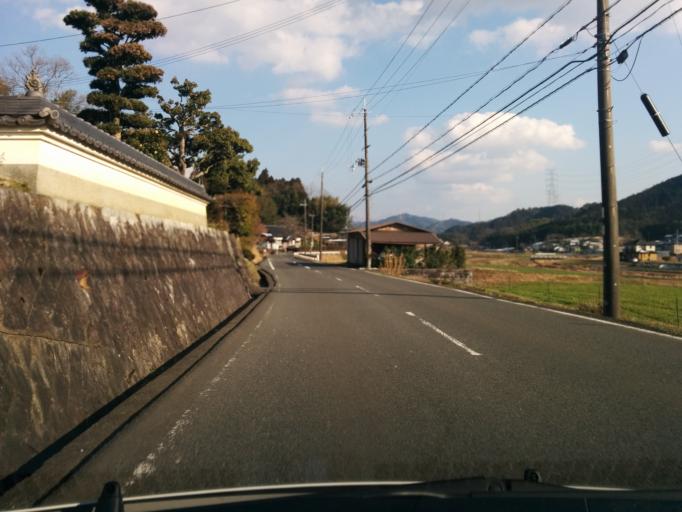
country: JP
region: Kyoto
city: Ayabe
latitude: 35.3669
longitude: 135.1976
